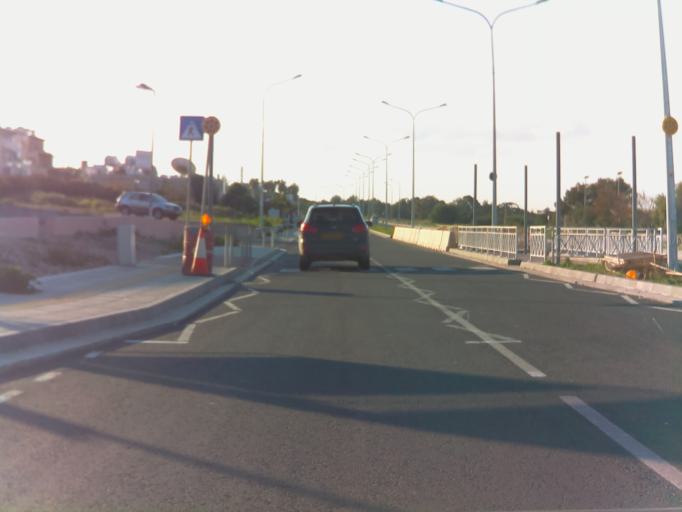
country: CY
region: Pafos
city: Chlorakas
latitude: 34.7812
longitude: 32.4060
